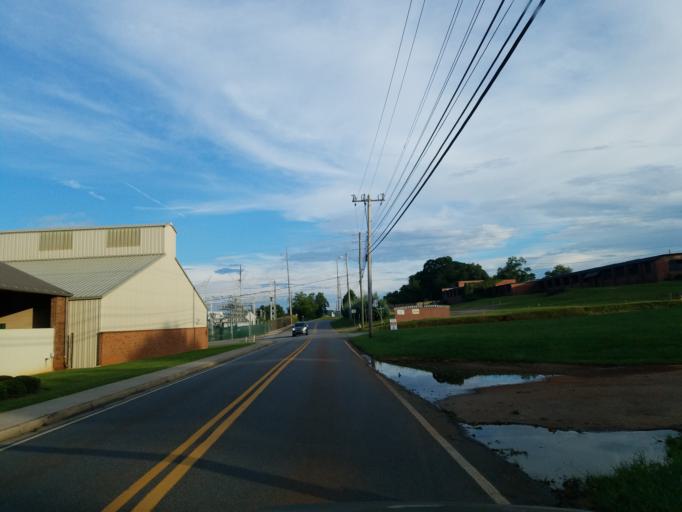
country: US
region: Georgia
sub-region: Bartow County
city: Cartersville
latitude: 34.1594
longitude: -84.7945
